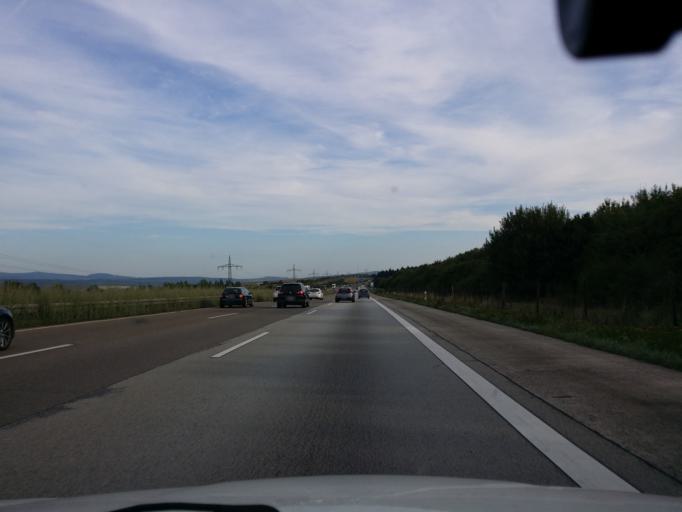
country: DE
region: Hesse
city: Bad Camberg
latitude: 50.3190
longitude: 8.2234
